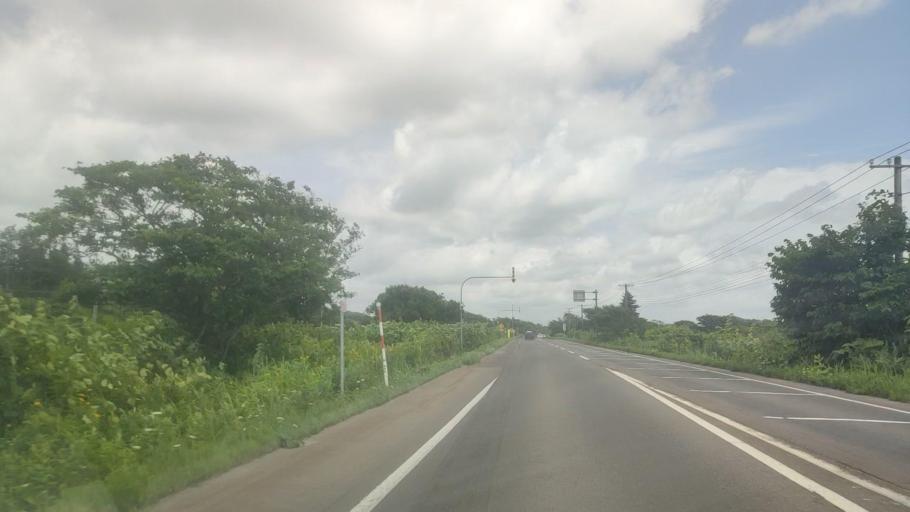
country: JP
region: Hokkaido
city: Niseko Town
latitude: 42.4562
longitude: 140.3334
